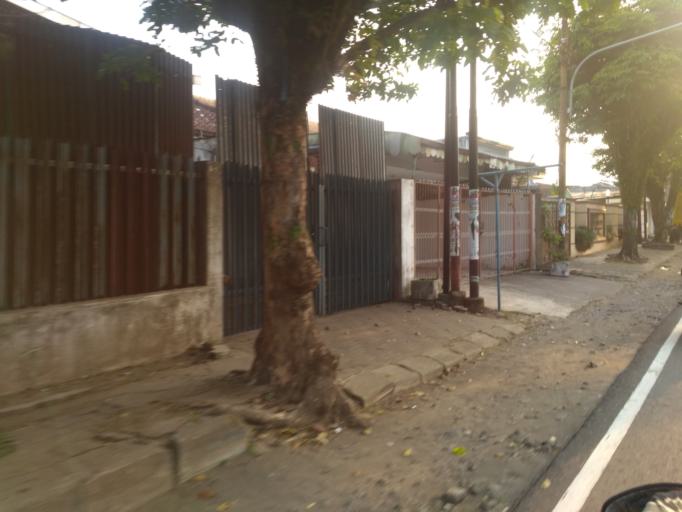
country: ID
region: East Java
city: Kepuh
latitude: -8.0008
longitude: 112.6192
